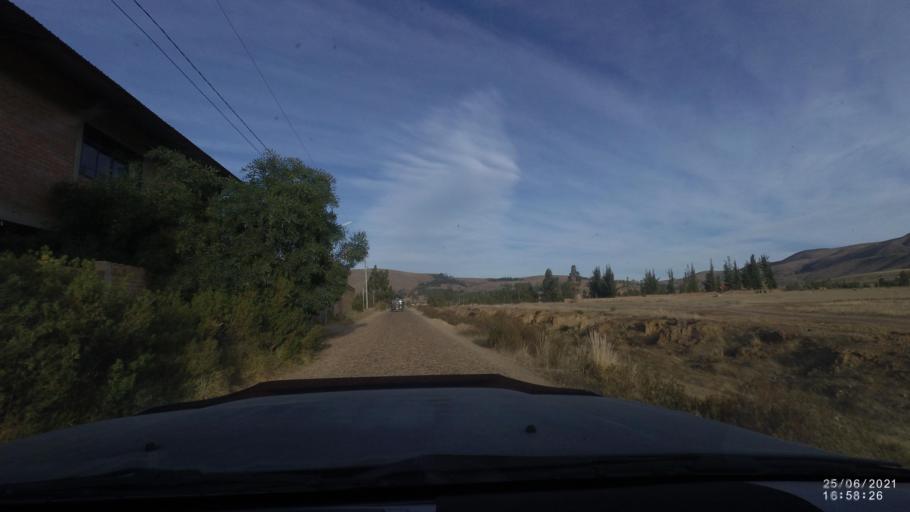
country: BO
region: Cochabamba
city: Arani
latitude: -17.8317
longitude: -65.7572
